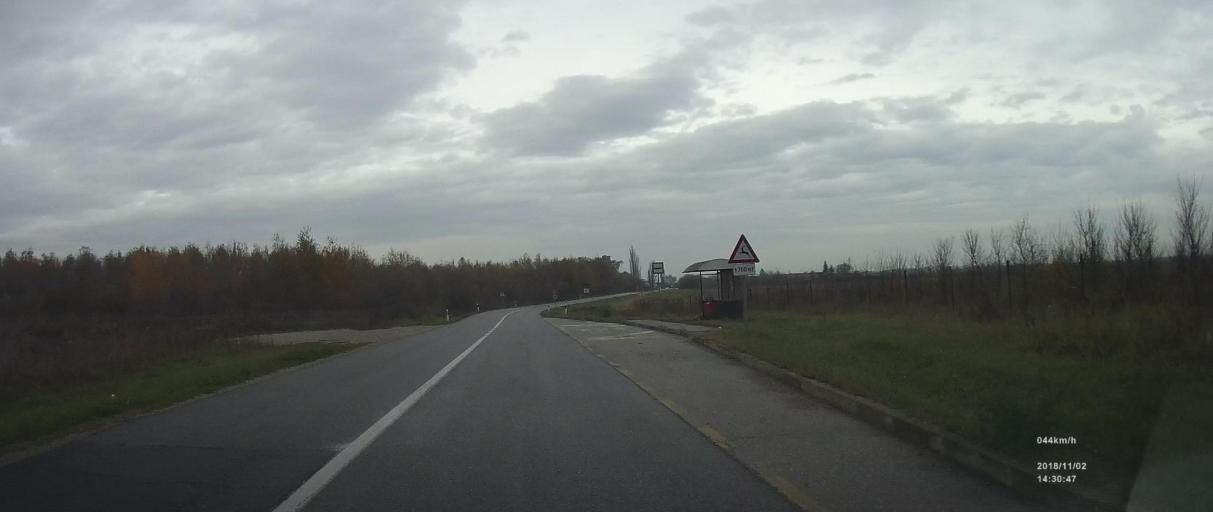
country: HR
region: Zagrebacka
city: Gradici
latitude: 45.6805
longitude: 16.0561
